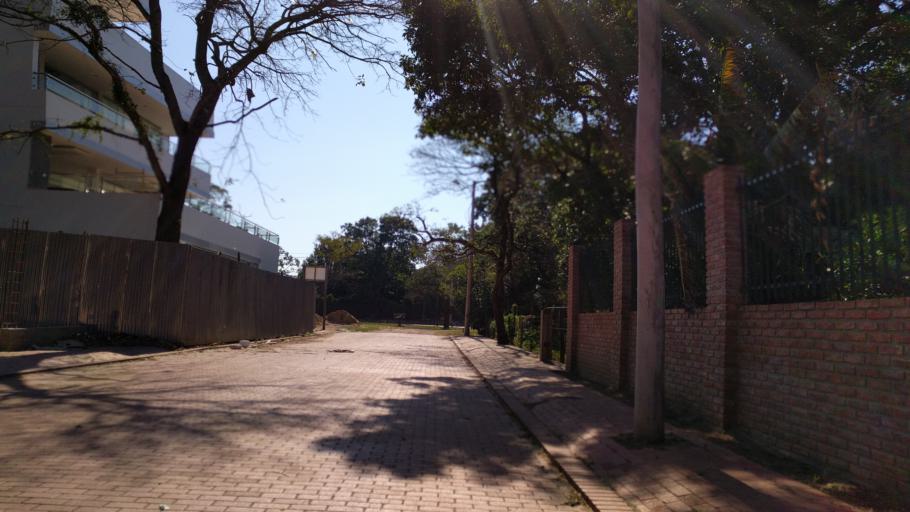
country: BO
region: Santa Cruz
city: Santa Cruz de la Sierra
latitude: -17.8083
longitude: -63.2238
